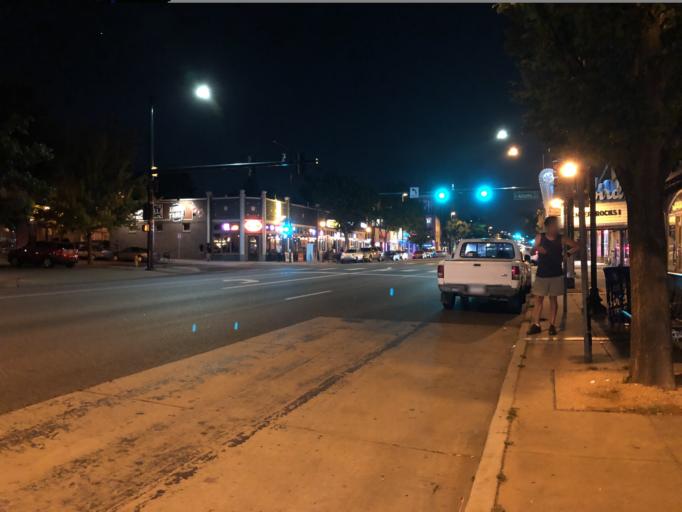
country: US
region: Colorado
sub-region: Denver County
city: Denver
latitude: 39.7403
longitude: -104.9480
